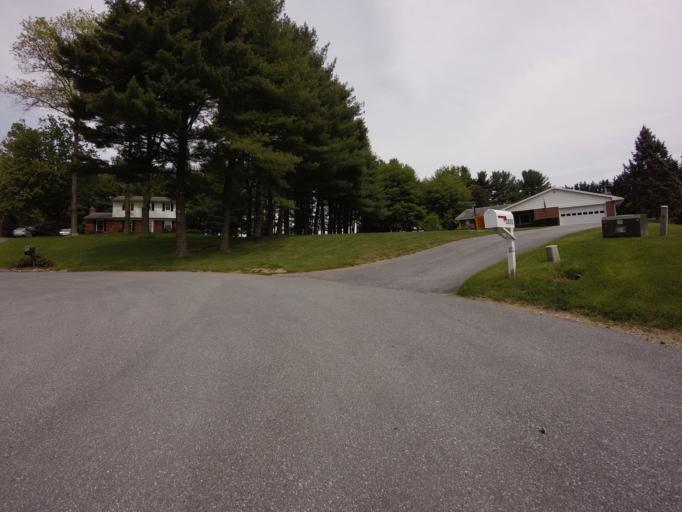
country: US
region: Maryland
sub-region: Carroll County
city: Eldersburg
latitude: 39.4606
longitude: -76.9556
